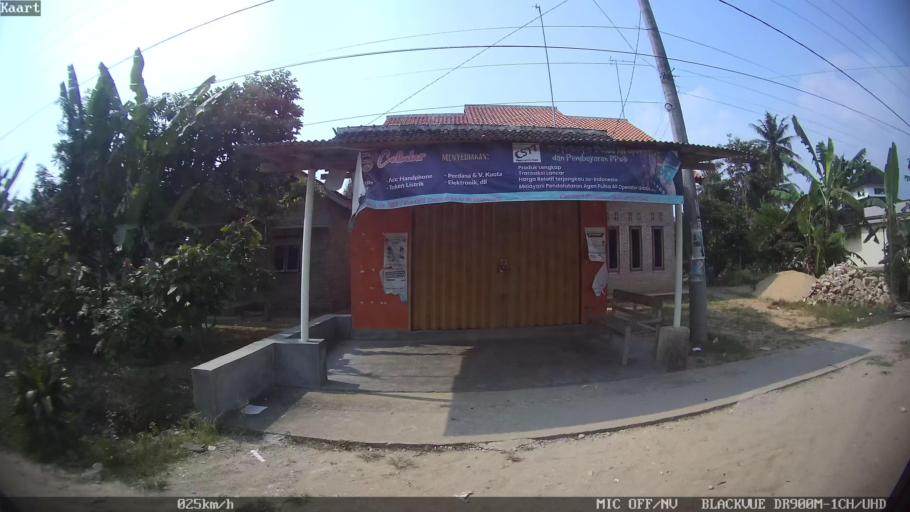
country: ID
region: Lampung
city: Kedondong
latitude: -5.4099
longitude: 104.9982
